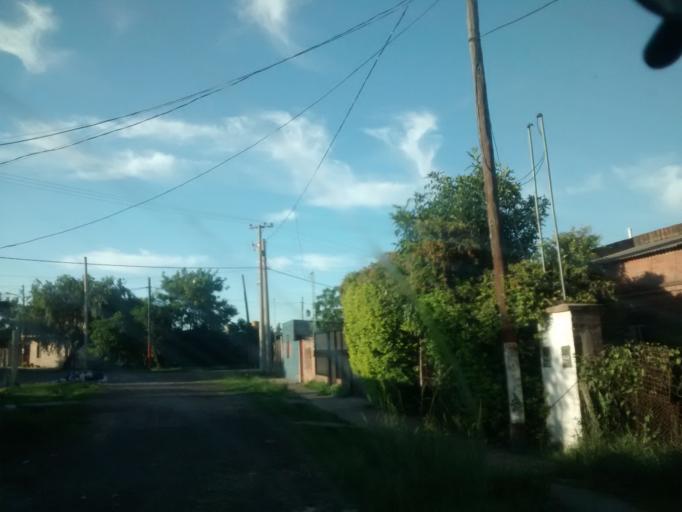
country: AR
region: Chaco
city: Resistencia
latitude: -27.4729
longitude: -58.9866
